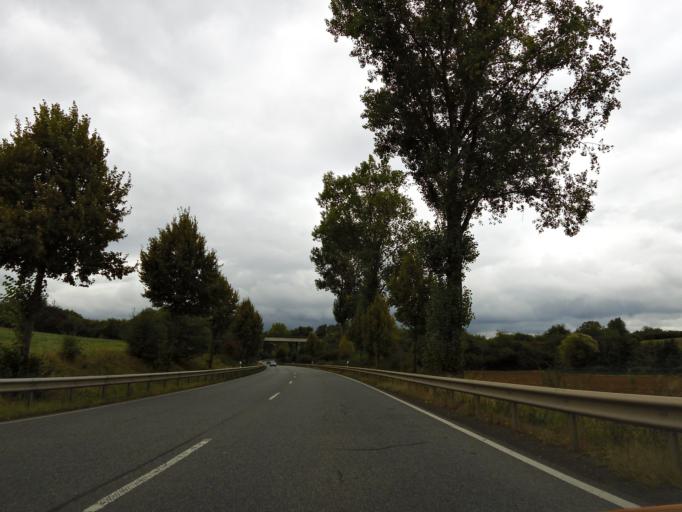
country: DE
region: Rheinland-Pfalz
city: Dreisen
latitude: 49.6004
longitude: 8.0225
